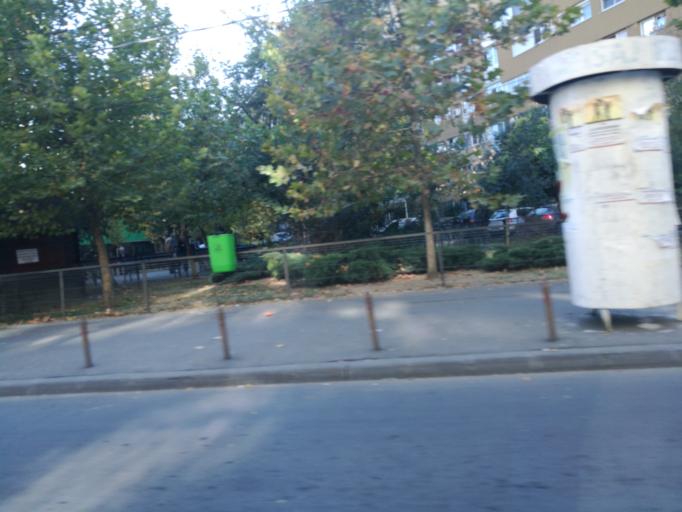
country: RO
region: Ilfov
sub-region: Comuna Chiajna
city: Rosu
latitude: 44.4366
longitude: 26.0340
